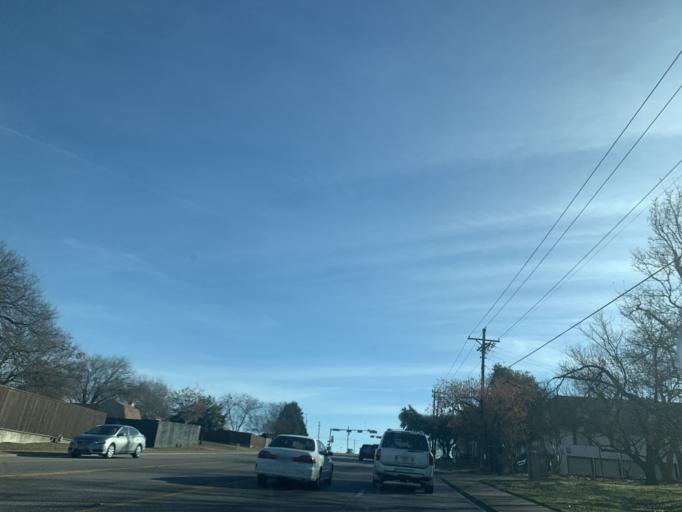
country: US
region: Texas
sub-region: Dallas County
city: DeSoto
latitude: 32.5896
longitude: -96.8477
